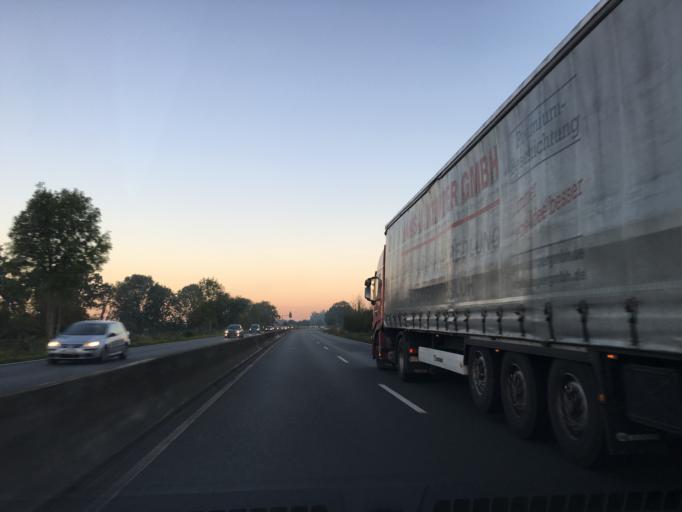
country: DE
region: North Rhine-Westphalia
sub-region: Regierungsbezirk Munster
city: Altenberge
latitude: 52.0030
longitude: 7.5162
